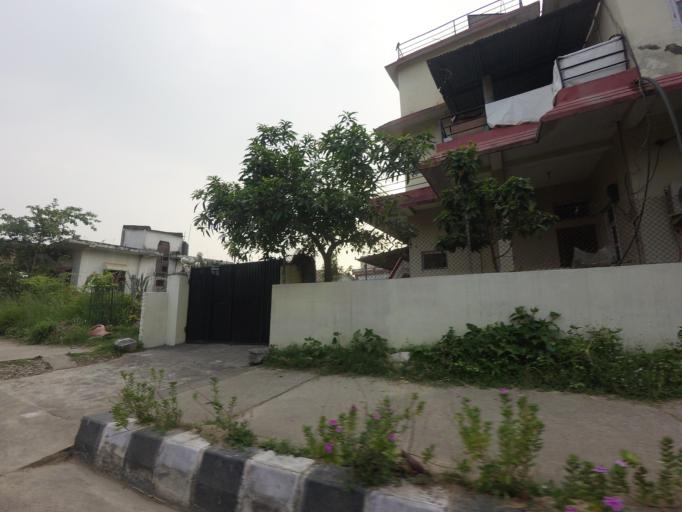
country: NP
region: Western Region
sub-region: Lumbini Zone
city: Bhairahawa
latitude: 27.4991
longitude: 83.4441
